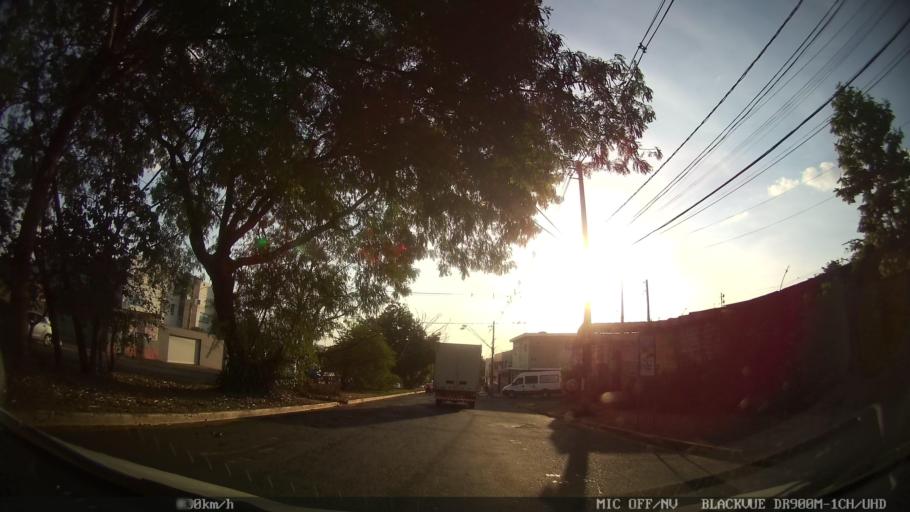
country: BR
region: Sao Paulo
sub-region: Ribeirao Preto
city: Ribeirao Preto
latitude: -21.1374
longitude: -47.7993
